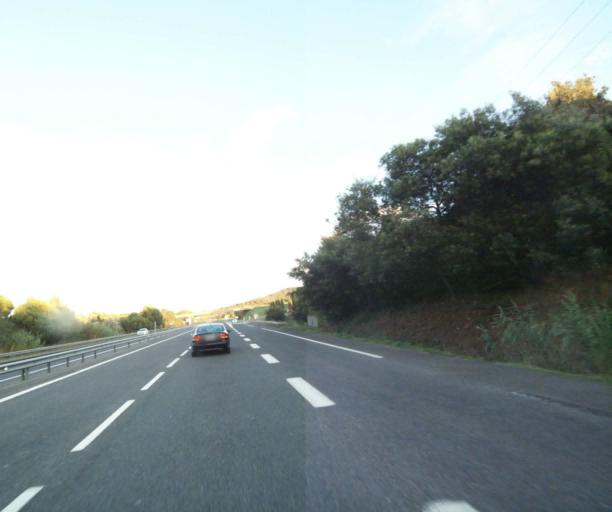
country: FR
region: Languedoc-Roussillon
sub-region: Departement des Pyrenees-Orientales
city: Argelers
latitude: 42.5371
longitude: 3.0297
